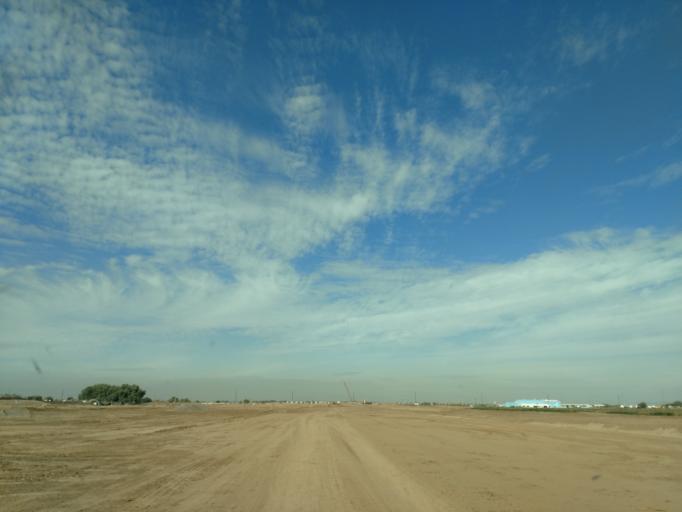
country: US
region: Arizona
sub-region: Maricopa County
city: Laveen
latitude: 33.3855
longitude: -112.1906
